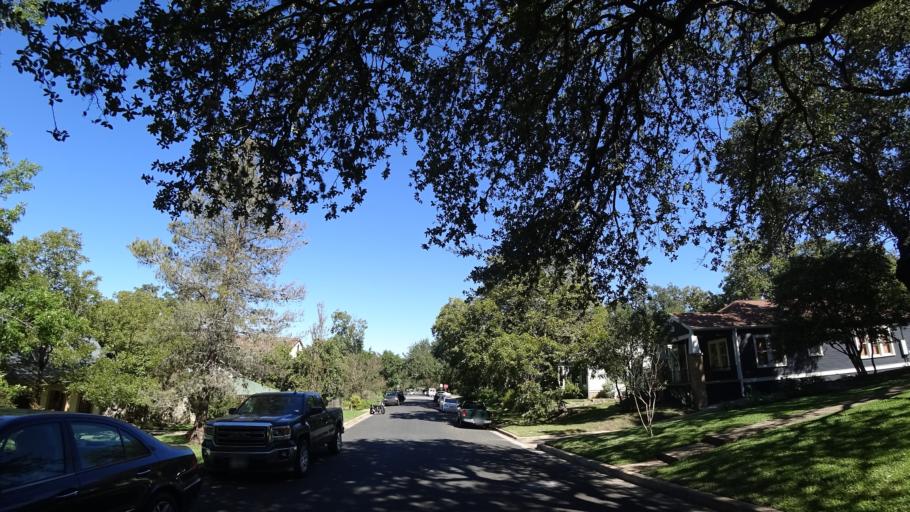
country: US
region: Texas
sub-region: Travis County
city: Austin
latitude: 30.2434
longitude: -97.7434
